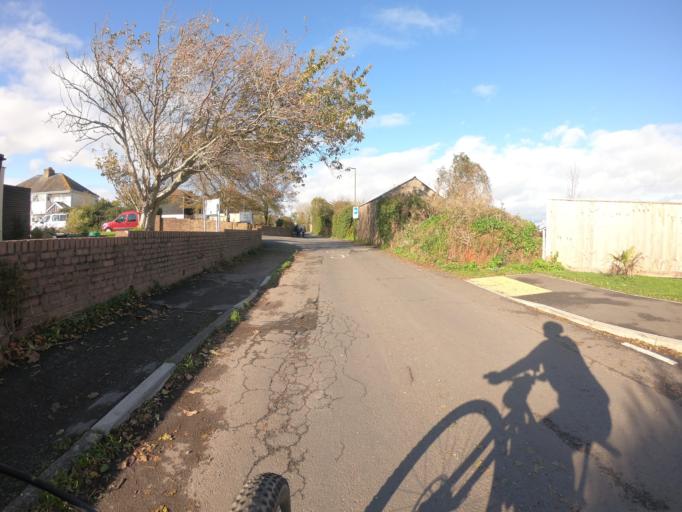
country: GB
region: England
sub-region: Borough of Torbay
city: Brixham
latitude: 50.3919
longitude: -3.5034
